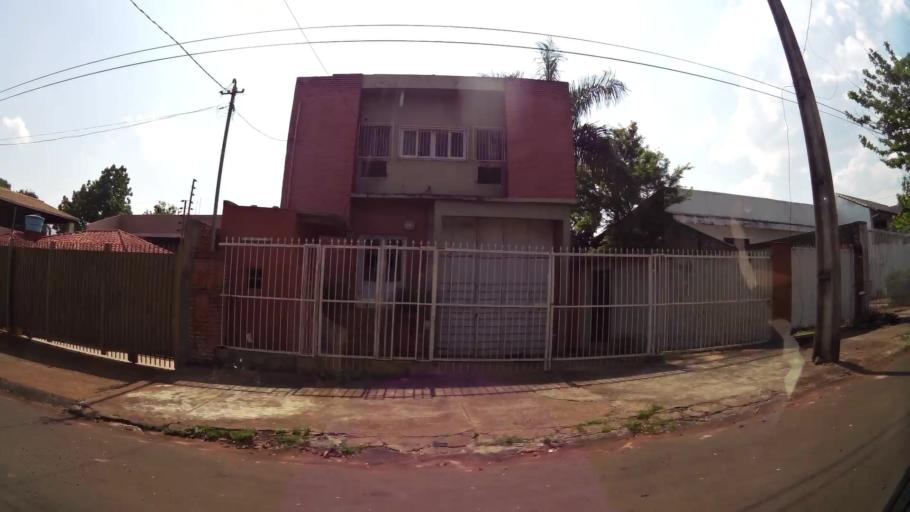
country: PY
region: Alto Parana
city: Ciudad del Este
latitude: -25.5126
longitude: -54.6293
